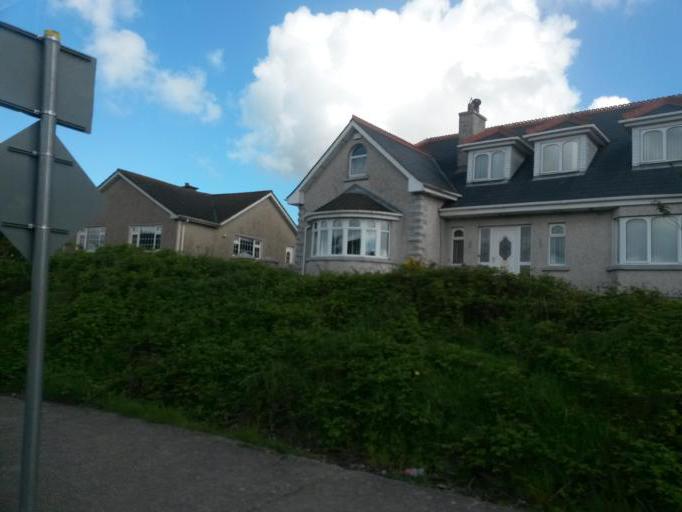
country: IE
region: Leinster
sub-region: Loch Garman
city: Enniscorthy
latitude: 52.4992
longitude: -6.5530
